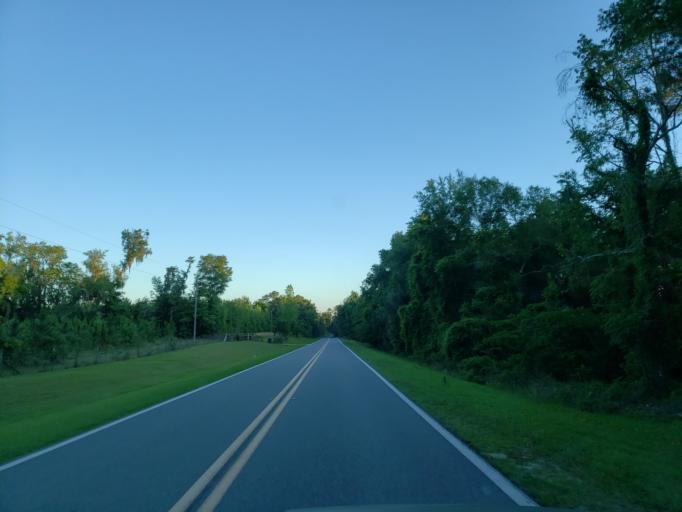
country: US
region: Florida
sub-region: Madison County
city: Madison
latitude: 30.6116
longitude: -83.2551
